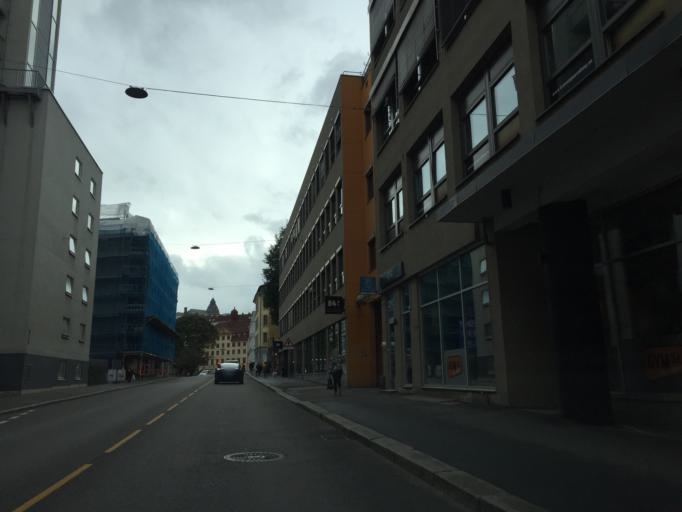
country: NO
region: Oslo
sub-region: Oslo
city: Oslo
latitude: 59.9283
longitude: 10.7538
